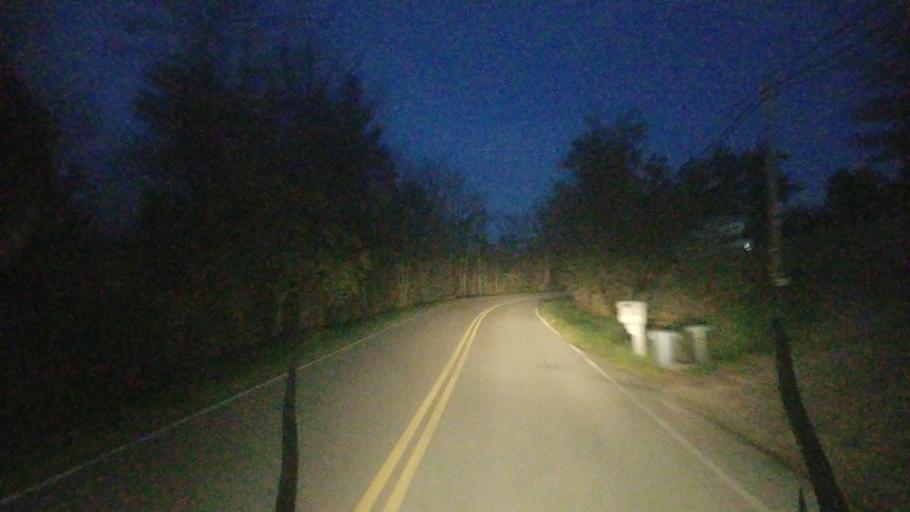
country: US
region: Ohio
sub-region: Belmont County
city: Barnesville
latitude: 40.0570
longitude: -81.2281
